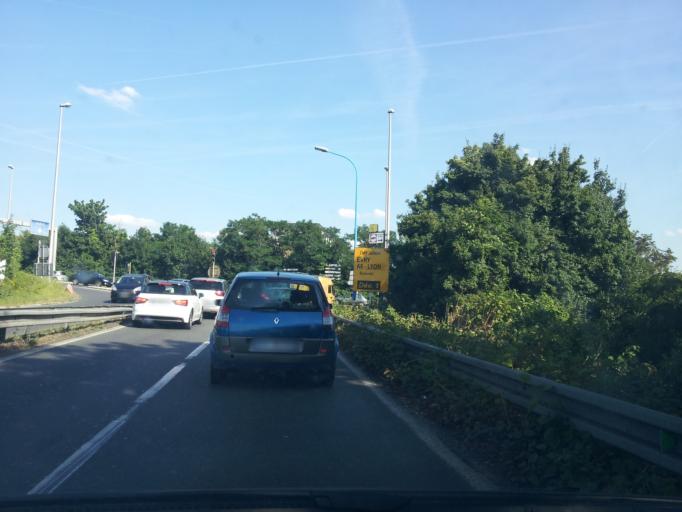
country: FR
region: Ile-de-France
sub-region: Departement de l'Essonne
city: Villemoisson-sur-Orge
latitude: 48.6772
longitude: 2.3370
